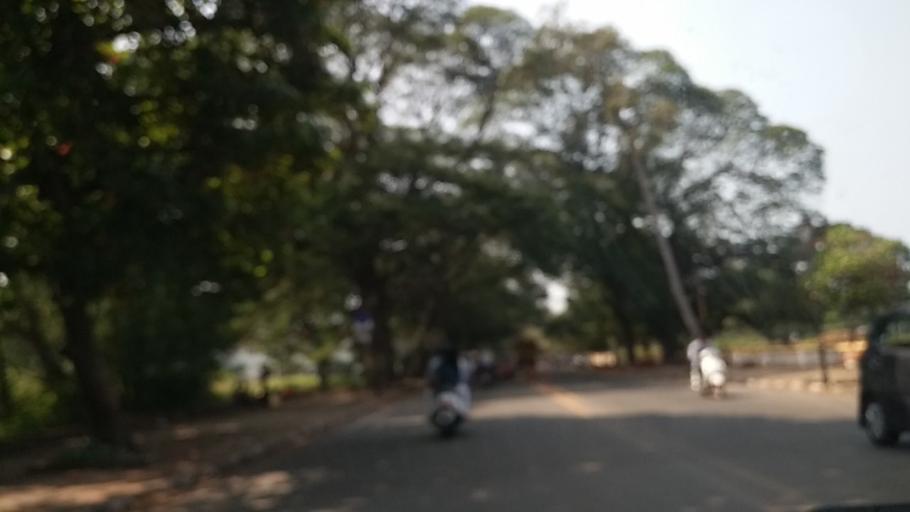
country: IN
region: Goa
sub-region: North Goa
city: Panaji
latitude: 15.4901
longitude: 73.8152
